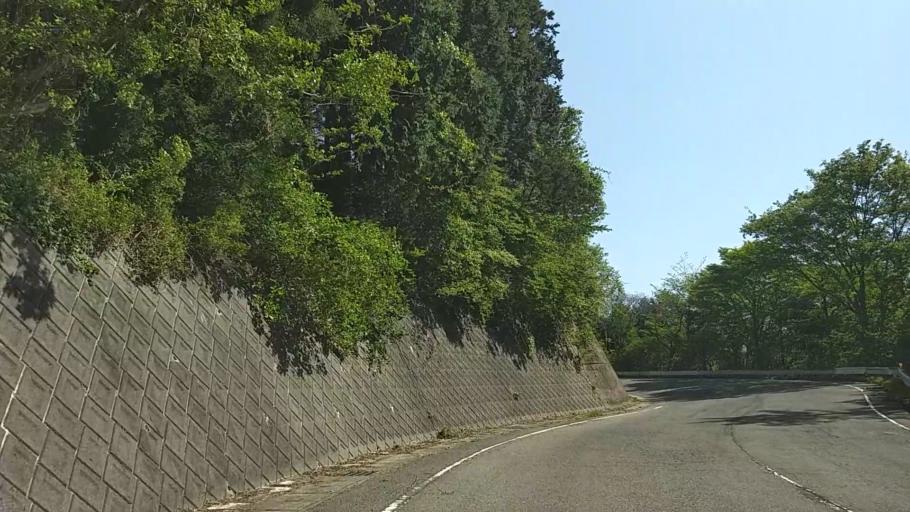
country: JP
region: Shizuoka
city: Gotemba
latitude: 35.2838
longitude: 138.9652
